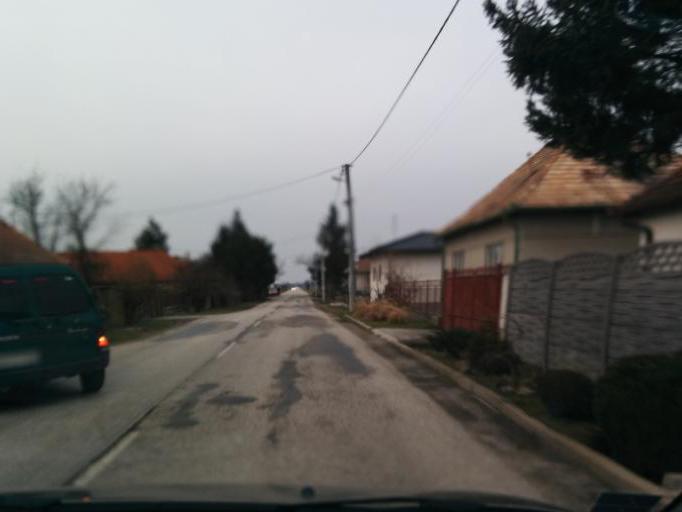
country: SK
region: Trnavsky
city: Sladkovicovo
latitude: 48.2241
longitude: 17.6353
